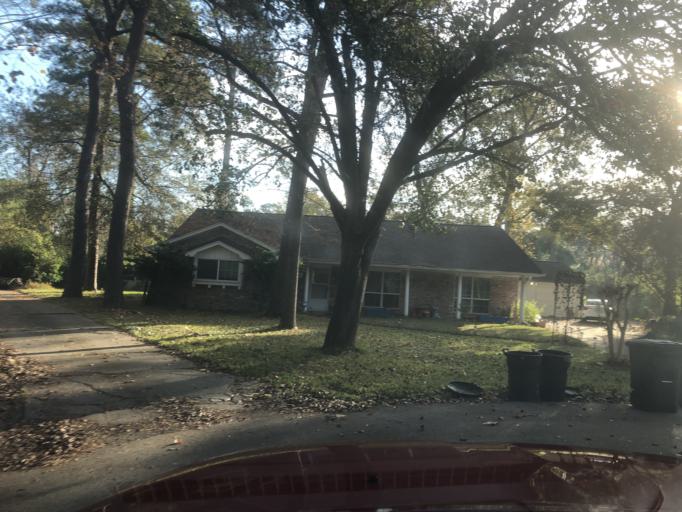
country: US
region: Texas
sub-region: Harris County
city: Spring
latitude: 30.0099
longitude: -95.4683
